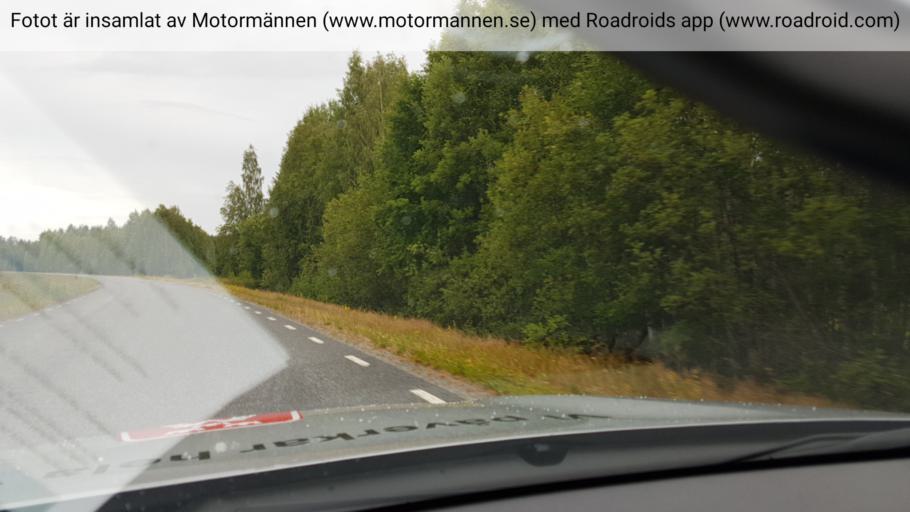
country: SE
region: Norrbotten
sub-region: Bodens Kommun
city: Boden
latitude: 65.8452
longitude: 21.4764
